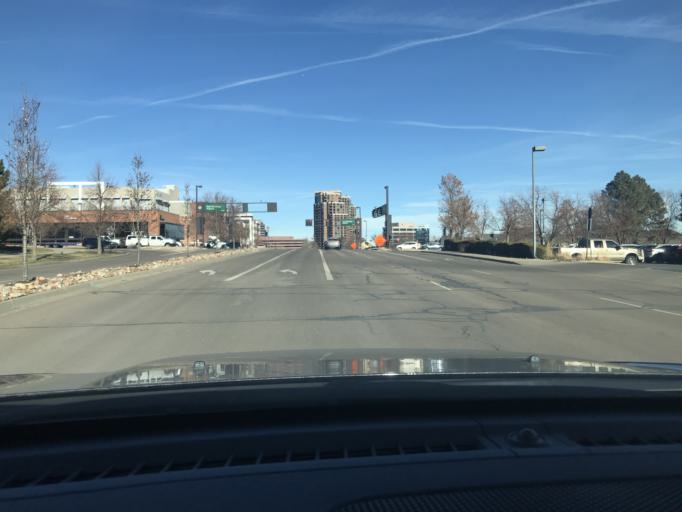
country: US
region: Colorado
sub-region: Arapahoe County
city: Castlewood
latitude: 39.6231
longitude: -104.8946
